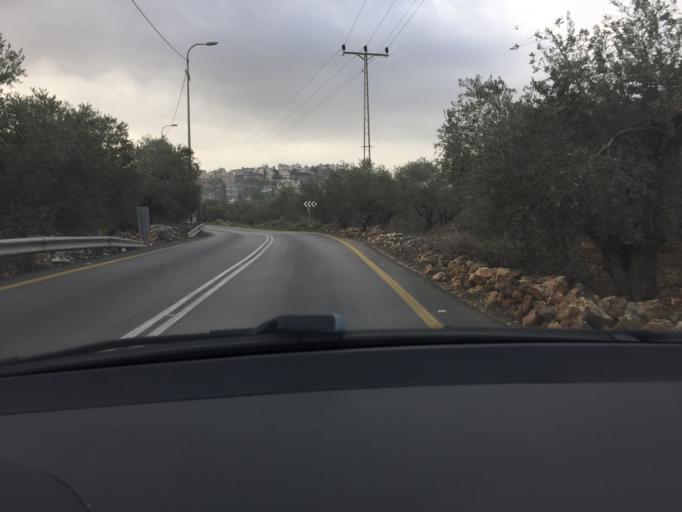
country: PS
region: West Bank
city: Al Lubban al Gharbi
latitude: 32.0425
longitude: 35.0412
